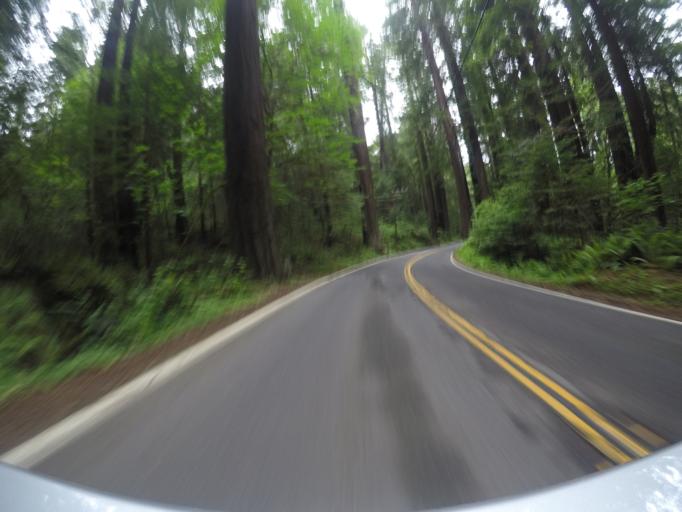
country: US
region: California
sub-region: Humboldt County
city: Rio Dell
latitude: 40.4172
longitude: -123.9756
